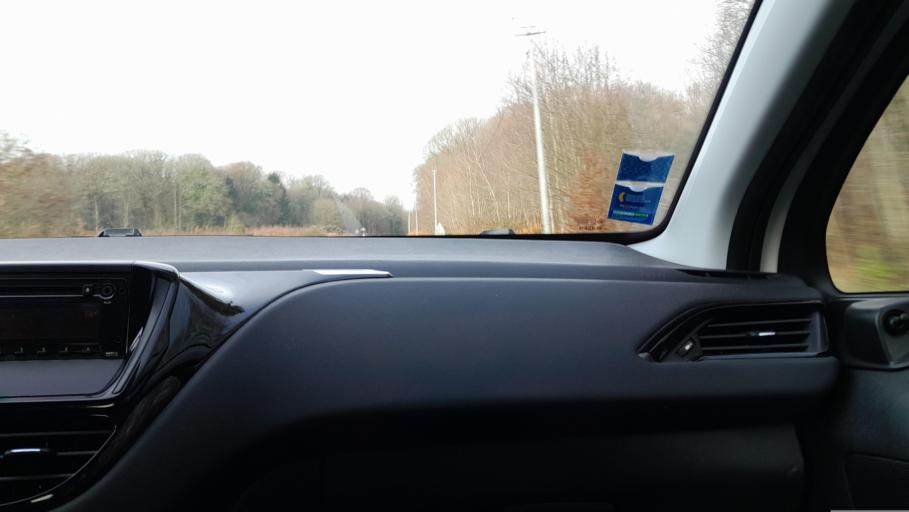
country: FR
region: Brittany
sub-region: Departement d'Ille-et-Vilaine
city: La Guerche-de-Bretagne
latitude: 47.9042
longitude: -1.1853
